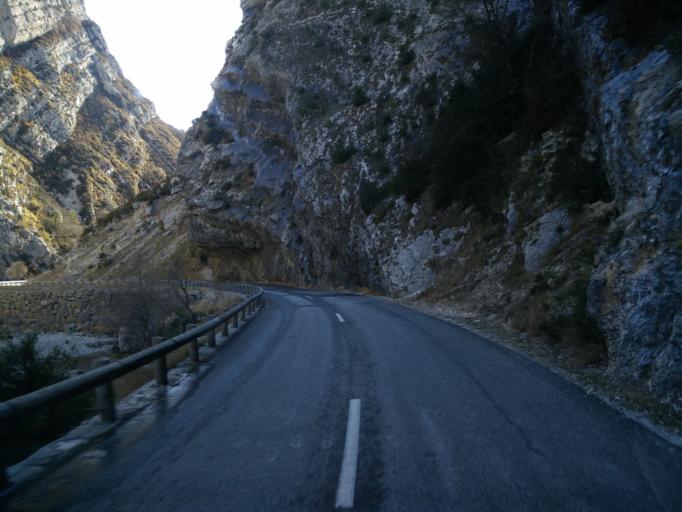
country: FR
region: Provence-Alpes-Cote d'Azur
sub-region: Departement des Alpes-de-Haute-Provence
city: Castellane
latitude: 43.8167
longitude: 6.4366
